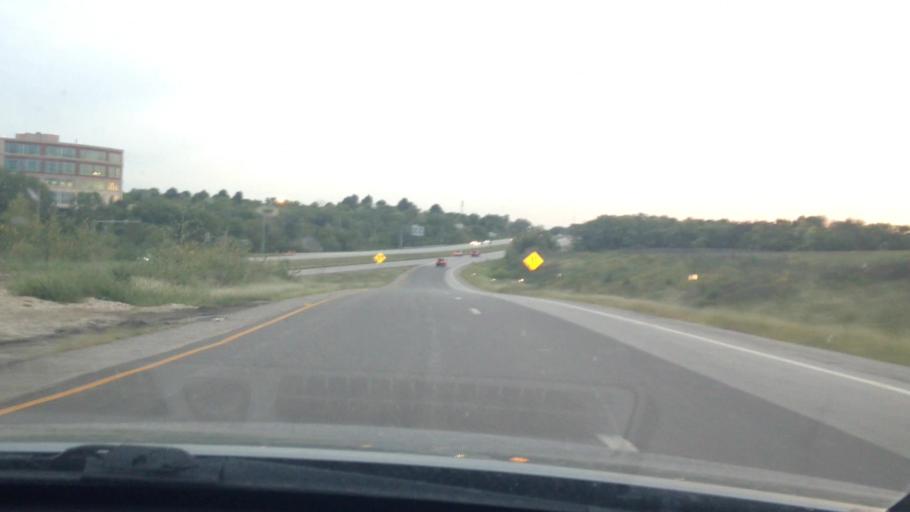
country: US
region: Missouri
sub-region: Jackson County
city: Lees Summit
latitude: 38.9452
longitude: -94.3784
